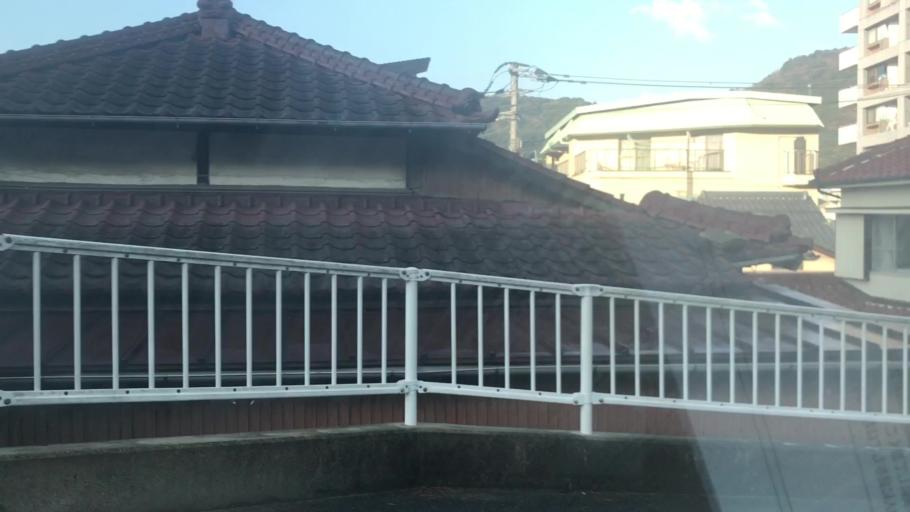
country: JP
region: Saga Prefecture
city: Takeocho-takeo
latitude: 33.1969
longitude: 130.0195
